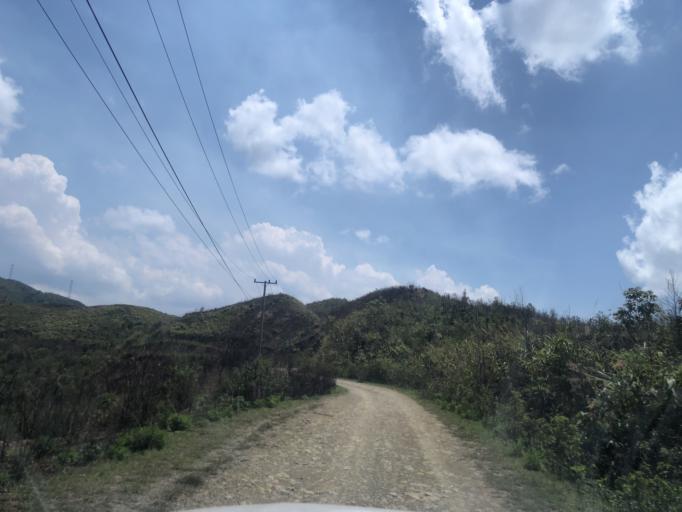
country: LA
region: Phongsali
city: Phongsali
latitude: 21.4064
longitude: 102.1862
